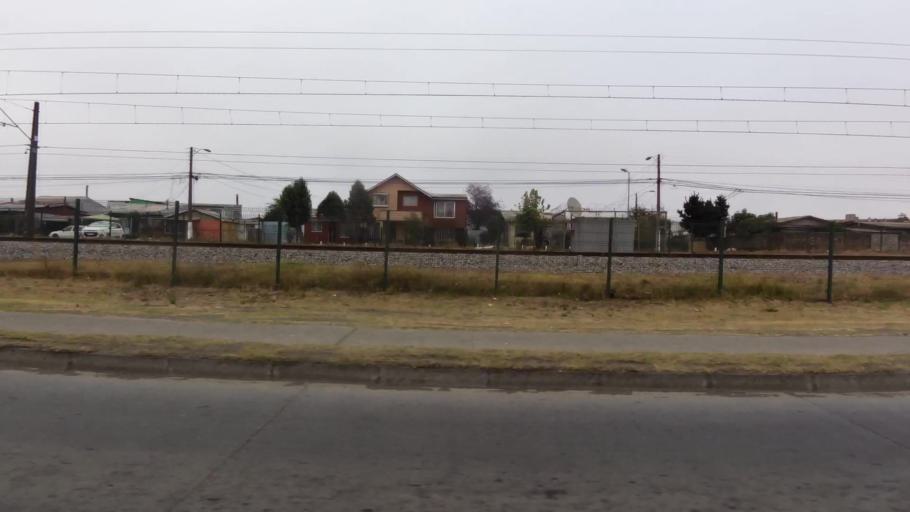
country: CL
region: Biobio
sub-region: Provincia de Concepcion
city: Concepcion
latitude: -36.7970
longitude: -73.0815
